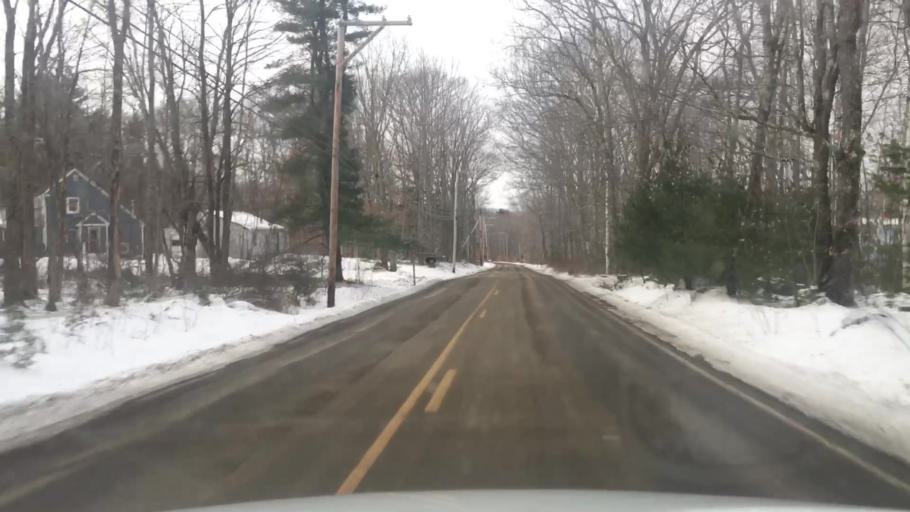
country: US
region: Maine
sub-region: Waldo County
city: Lincolnville
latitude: 44.2900
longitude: -69.0693
